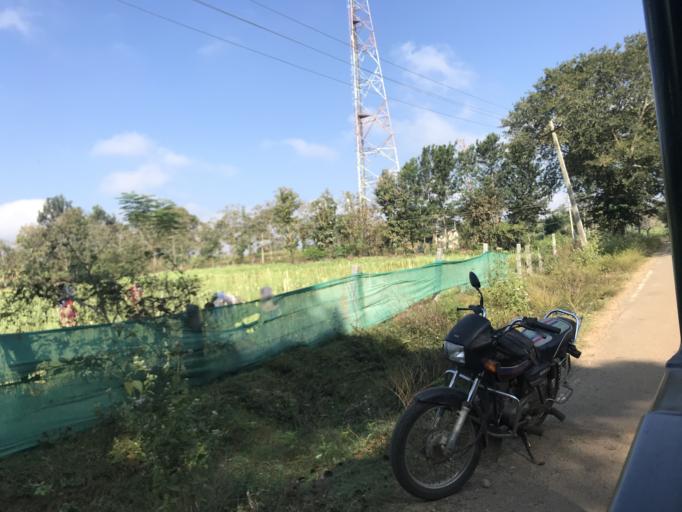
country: IN
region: Karnataka
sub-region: Mysore
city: Sargur
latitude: 11.9416
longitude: 76.2689
